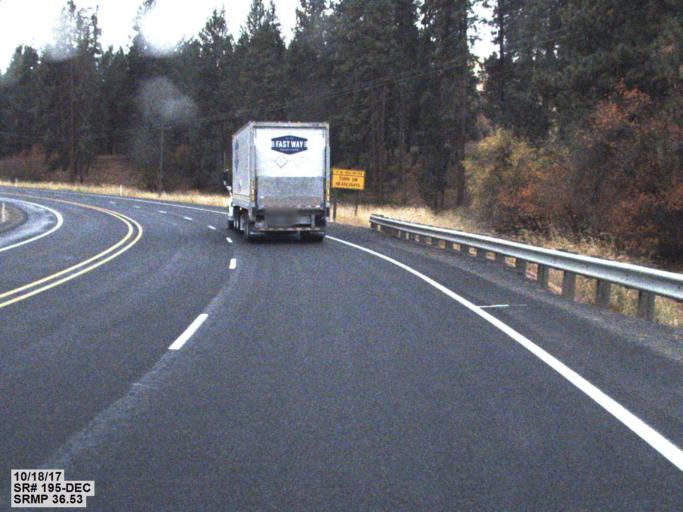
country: US
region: Washington
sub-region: Whitman County
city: Colfax
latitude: 46.8664
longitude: -117.3570
